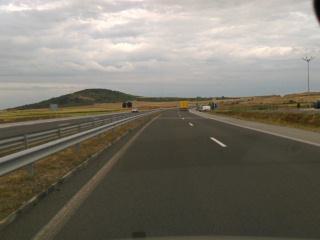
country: BG
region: Yambol
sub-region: Obshtina Yambol
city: Yambol
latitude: 42.5450
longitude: 26.4502
